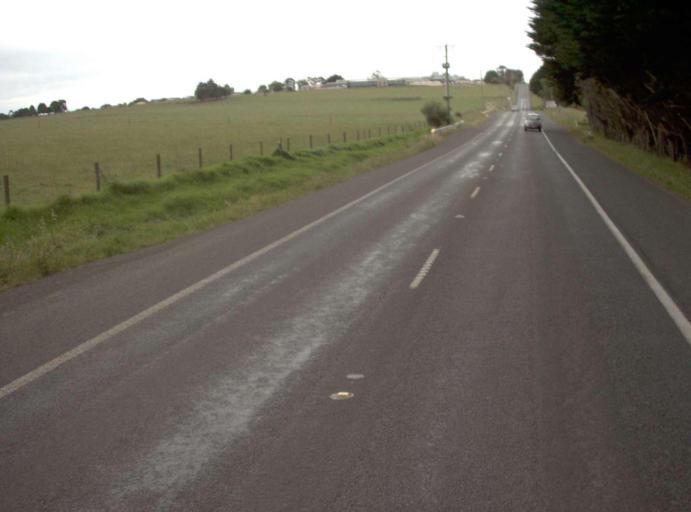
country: AU
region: Victoria
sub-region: Baw Baw
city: Warragul
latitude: -38.4950
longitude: 145.9520
